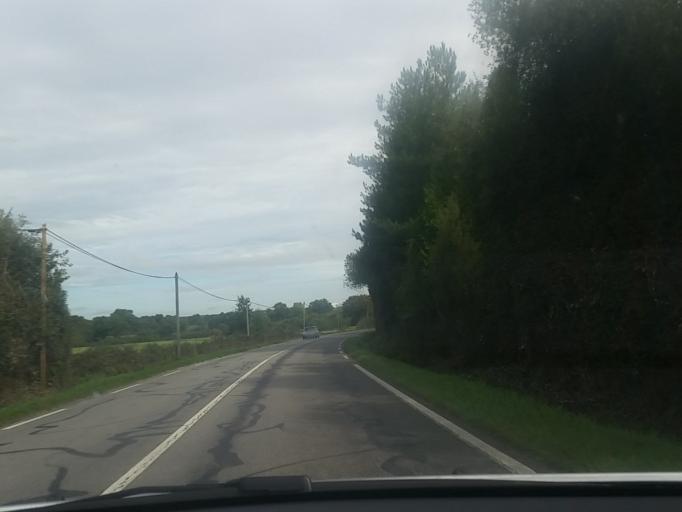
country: FR
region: Pays de la Loire
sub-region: Departement de la Loire-Atlantique
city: Chateaubriant
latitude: 47.7554
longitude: -1.3587
